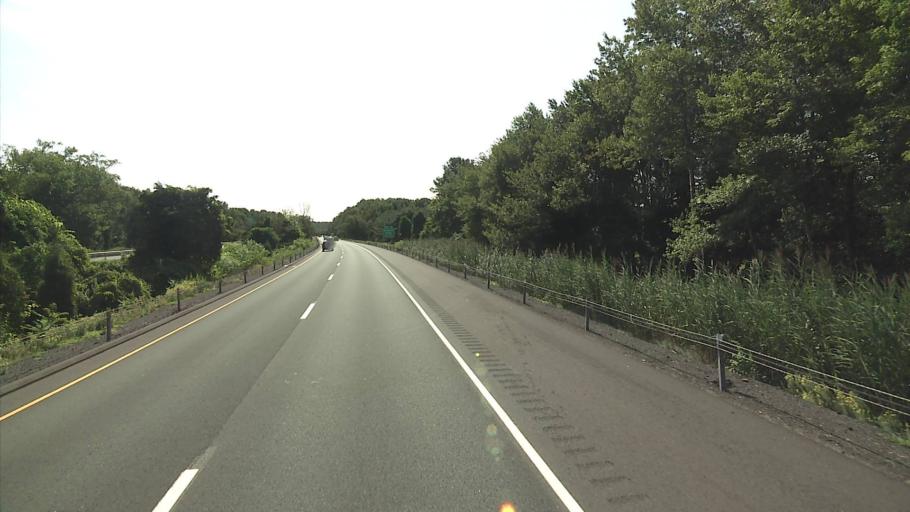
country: US
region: Connecticut
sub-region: Hartford County
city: Glastonbury Center
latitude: 41.7081
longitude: -72.5815
